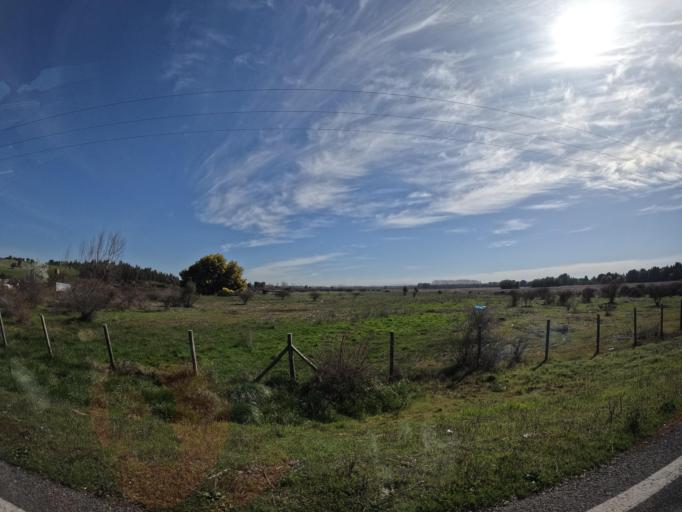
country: CL
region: Biobio
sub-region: Provincia de Biobio
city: Cabrero
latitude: -37.0096
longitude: -72.3642
